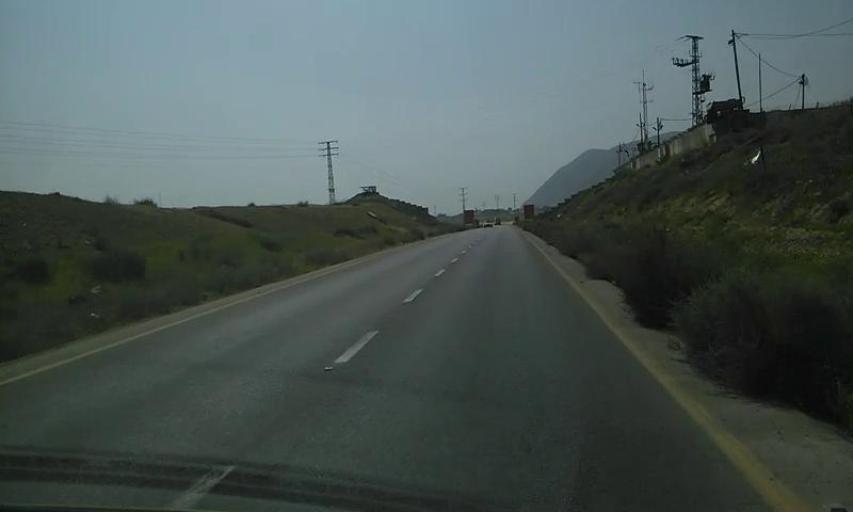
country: PS
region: West Bank
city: An Nuway`imah
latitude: 31.9044
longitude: 35.4243
